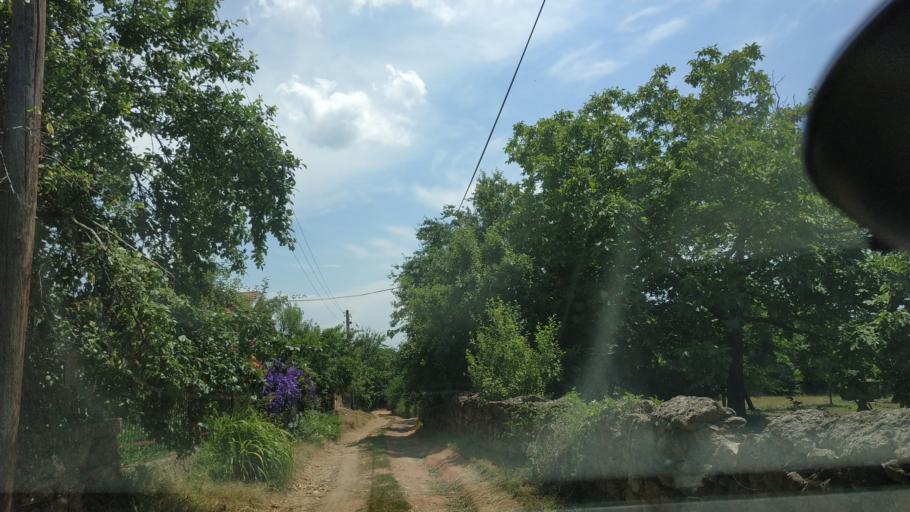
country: RS
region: Central Serbia
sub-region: Nisavski Okrug
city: Aleksinac
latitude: 43.5979
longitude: 21.6933
